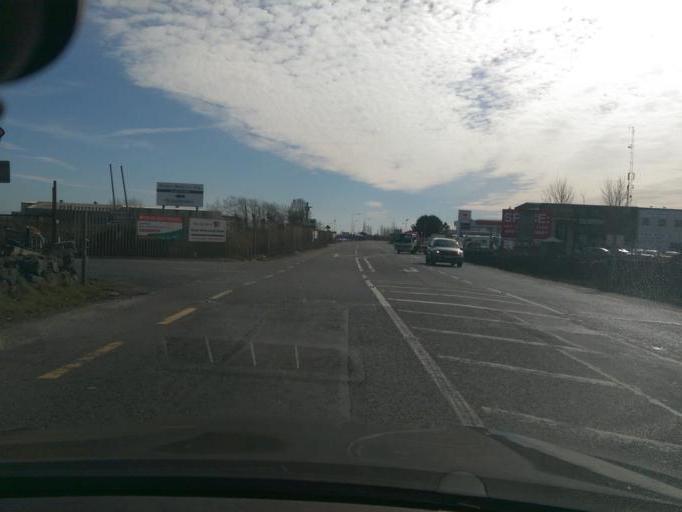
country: IE
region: Connaught
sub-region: County Galway
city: Oranmore
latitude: 53.2824
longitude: -8.9259
